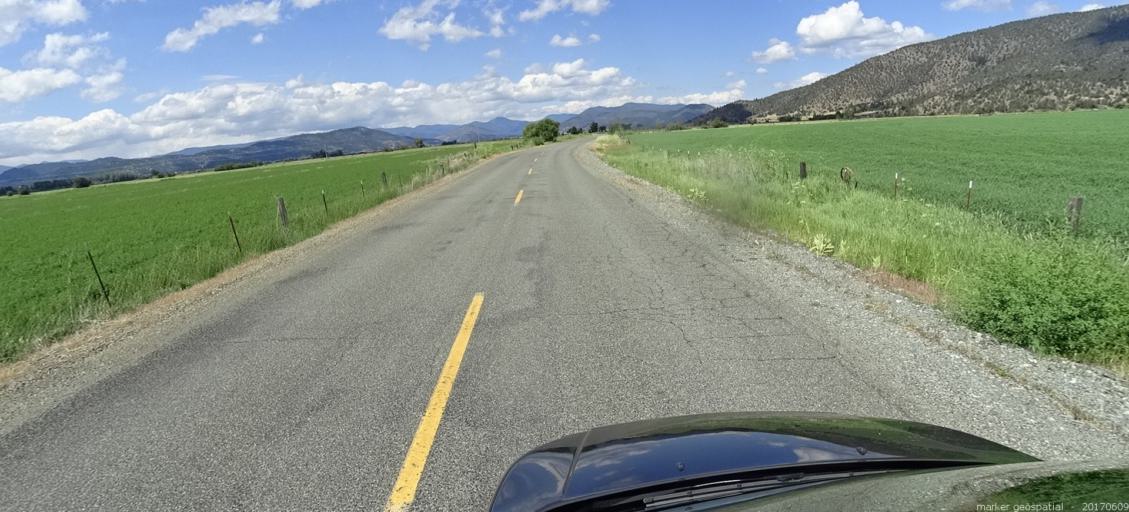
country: US
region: California
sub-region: Siskiyou County
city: Yreka
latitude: 41.5017
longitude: -122.8585
